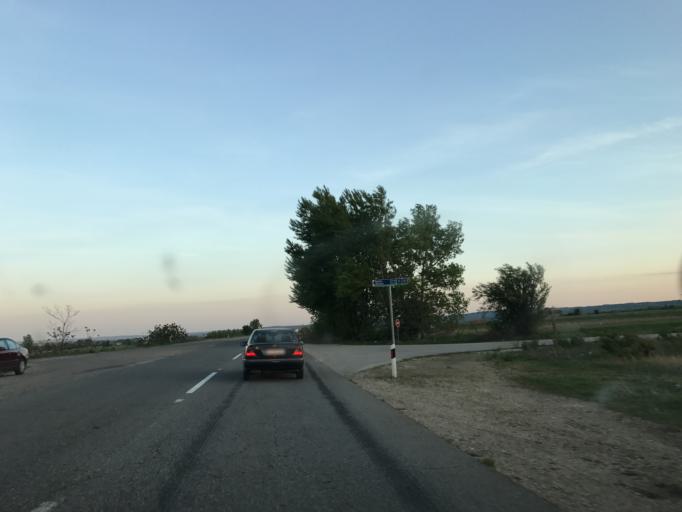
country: RS
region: Central Serbia
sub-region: Borski Okrug
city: Negotin
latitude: 44.2624
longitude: 22.5174
